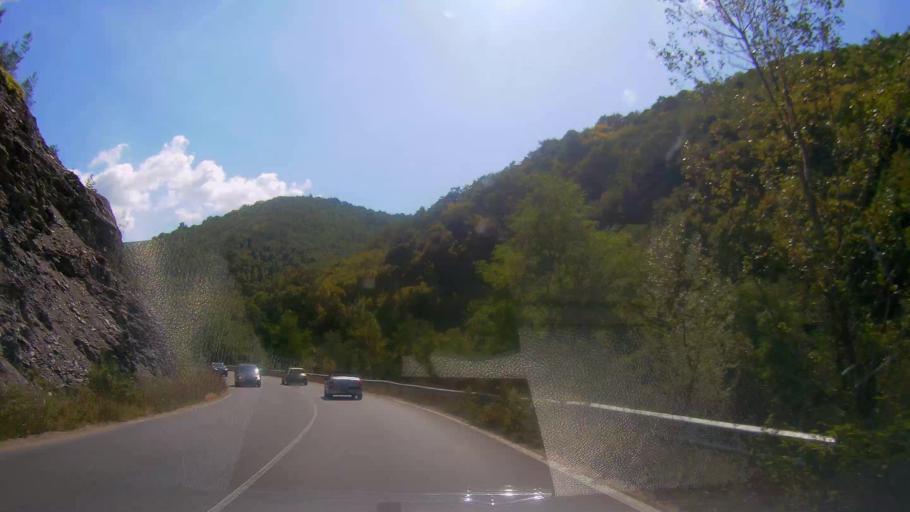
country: BG
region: Stara Zagora
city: Gurkovo
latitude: 42.7106
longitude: 25.7167
